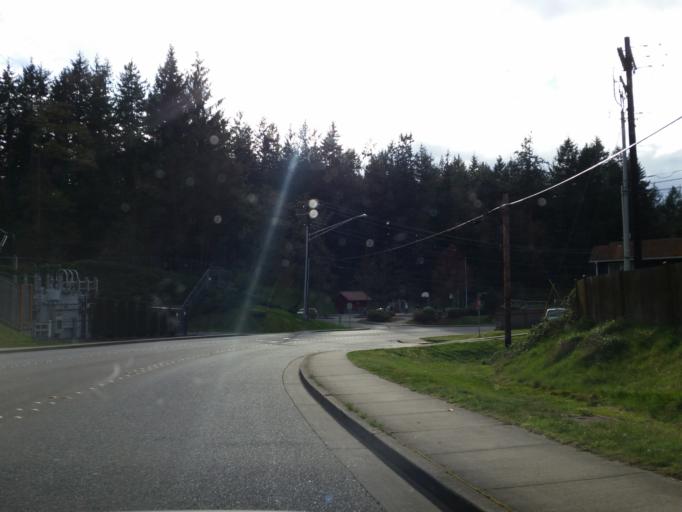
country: US
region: Washington
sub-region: Snohomish County
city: Lynnwood
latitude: 47.8305
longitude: -122.3313
